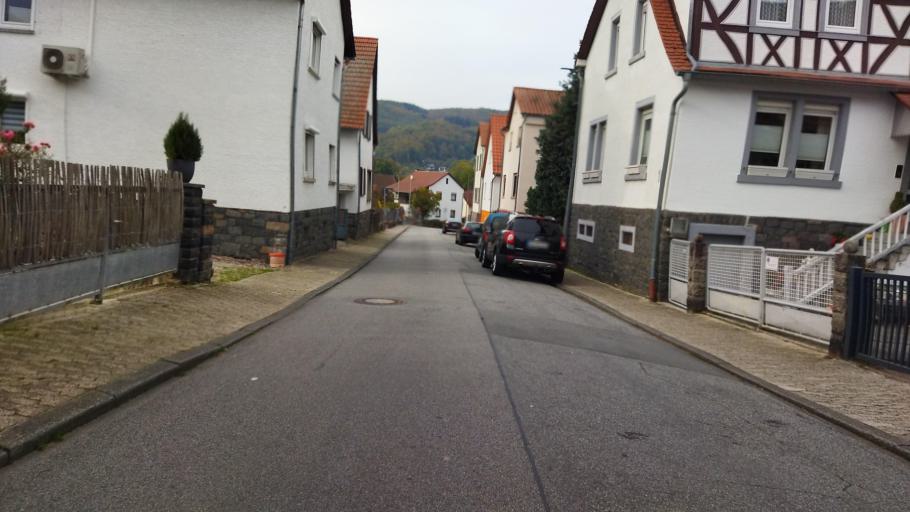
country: DE
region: Hesse
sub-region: Regierungsbezirk Darmstadt
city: Seeheim-Jugenheim
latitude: 49.7113
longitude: 8.6970
